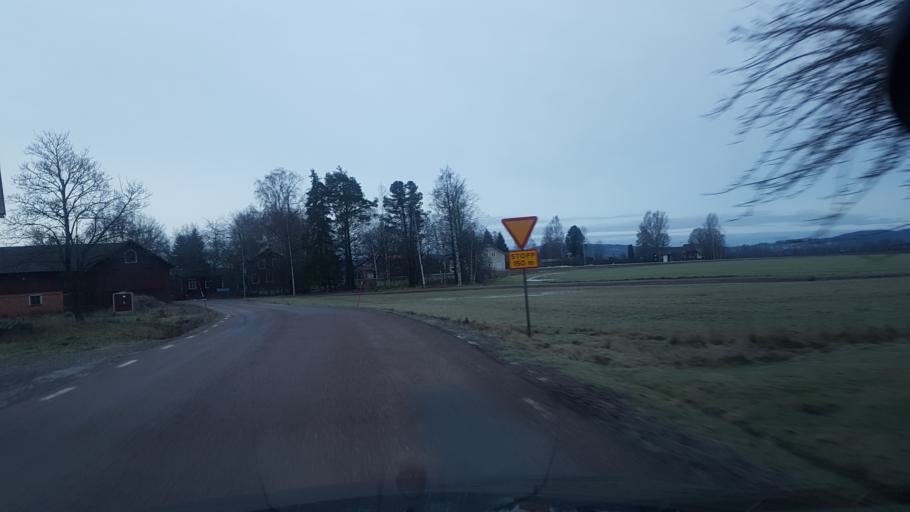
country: SE
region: Dalarna
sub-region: Saters Kommun
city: Saeter
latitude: 60.4243
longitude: 15.6560
